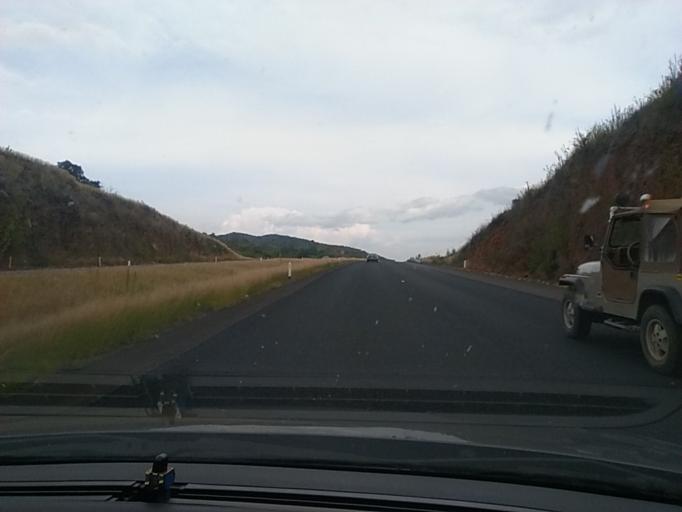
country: MX
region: Mexico
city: Huaniqueo de Morales
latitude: 19.8839
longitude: -101.4305
